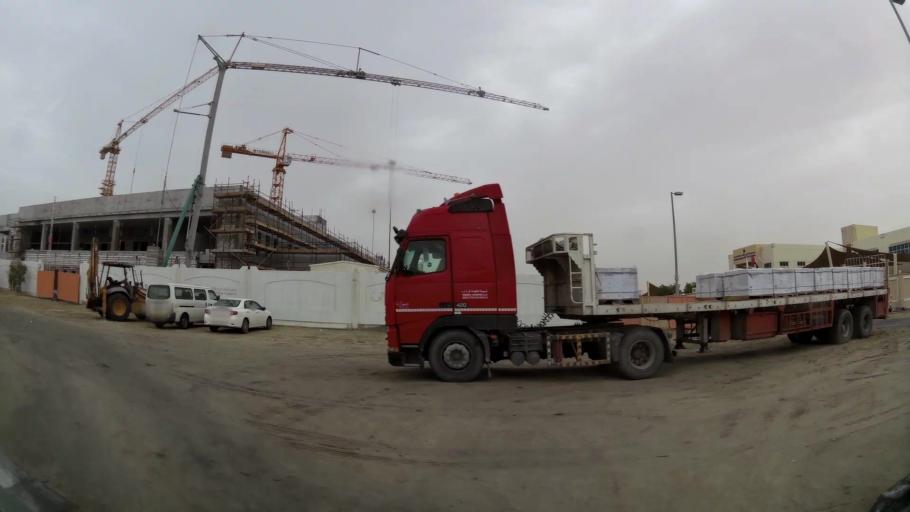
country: AE
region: Abu Dhabi
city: Abu Dhabi
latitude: 24.4291
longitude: 54.5831
